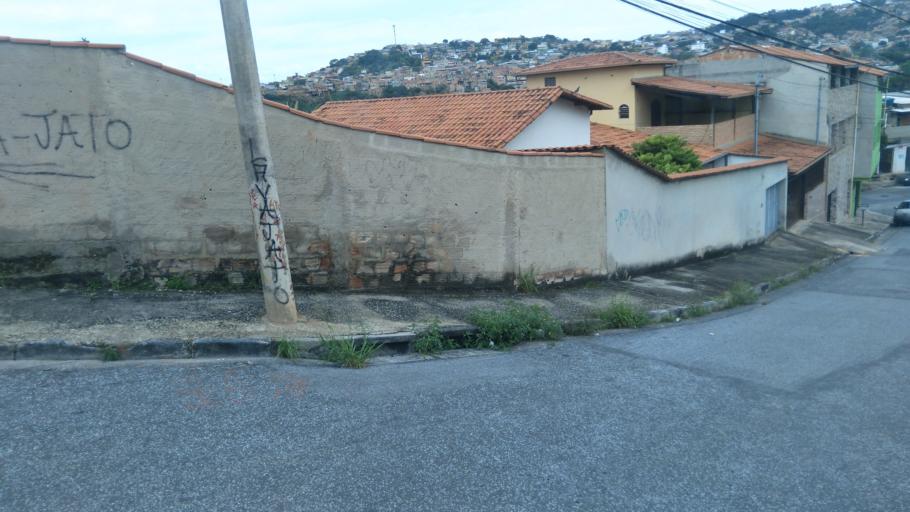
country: BR
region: Minas Gerais
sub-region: Belo Horizonte
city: Belo Horizonte
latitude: -19.8471
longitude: -43.9065
